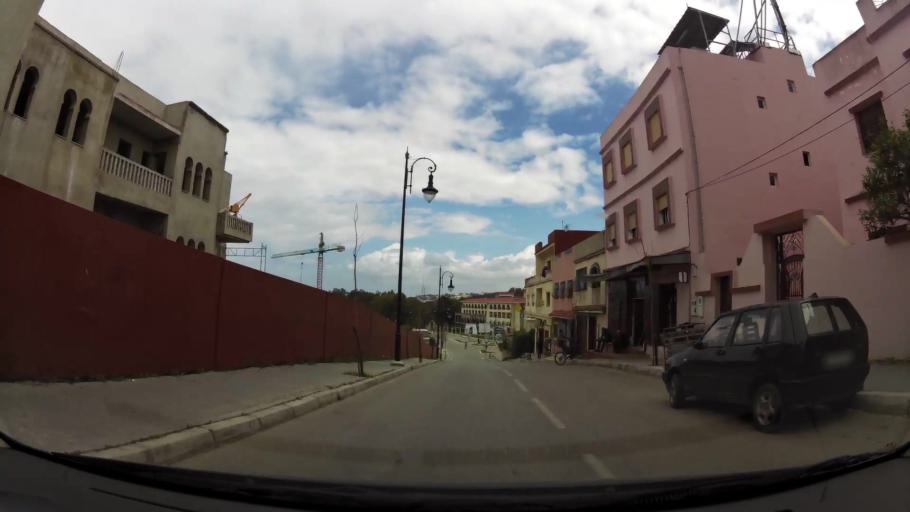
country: MA
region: Tanger-Tetouan
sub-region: Tanger-Assilah
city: Boukhalef
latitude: 35.7718
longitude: -5.8606
